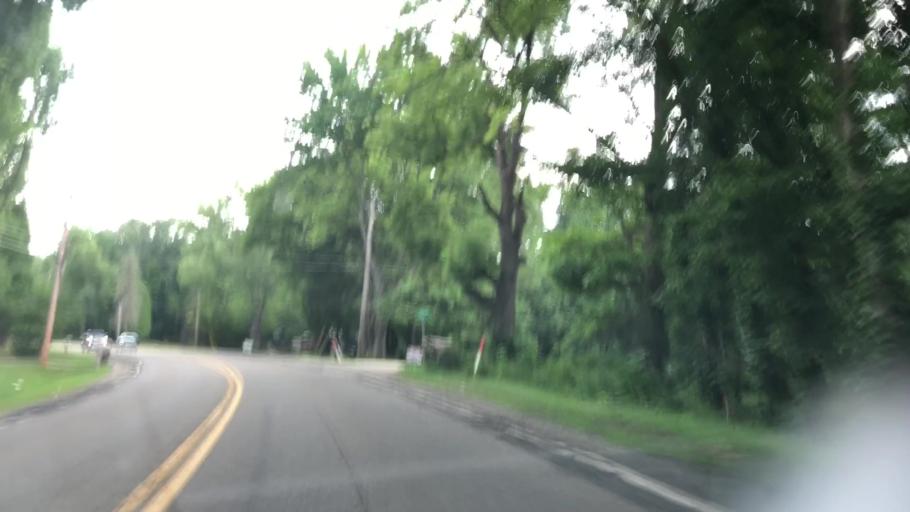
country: US
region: Ohio
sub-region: Summit County
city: New Franklin
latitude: 40.9708
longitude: -81.5205
